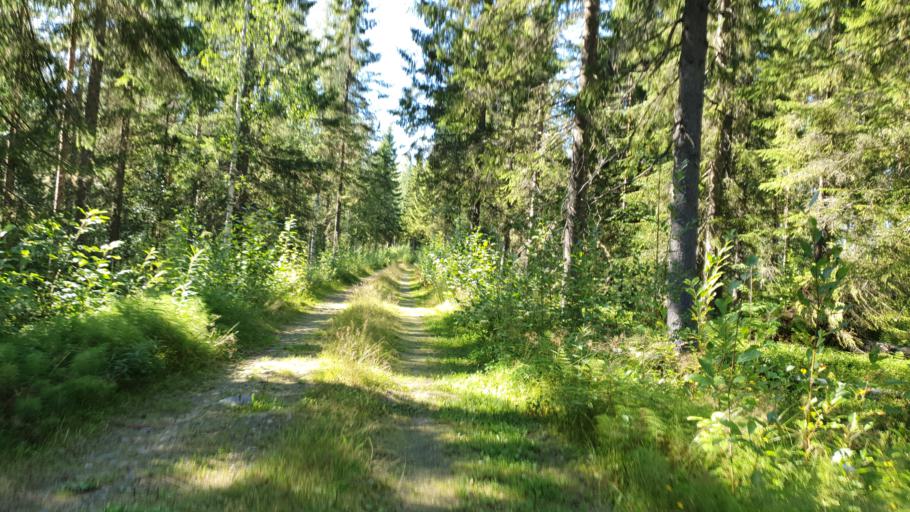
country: FI
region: Kainuu
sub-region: Kehys-Kainuu
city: Kuhmo
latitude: 64.1259
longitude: 29.4771
